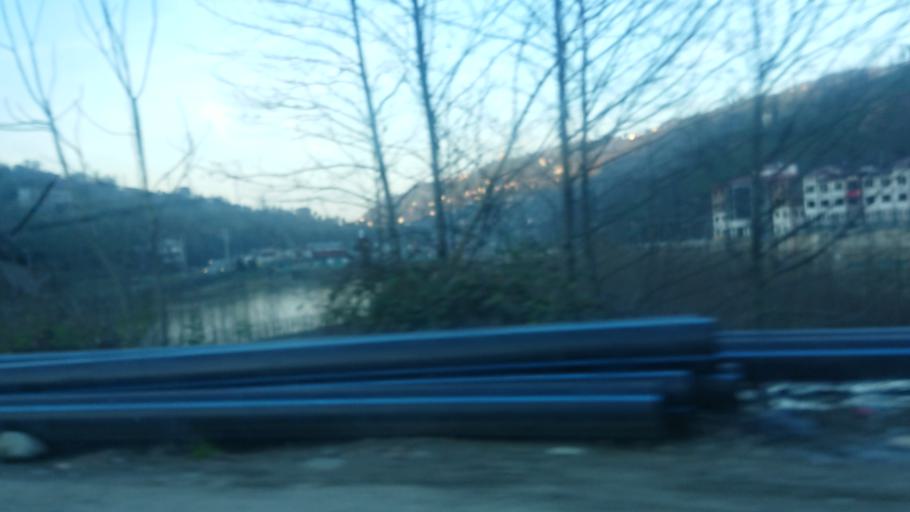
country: TR
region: Rize
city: Gundogdu
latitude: 41.0193
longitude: 40.5755
